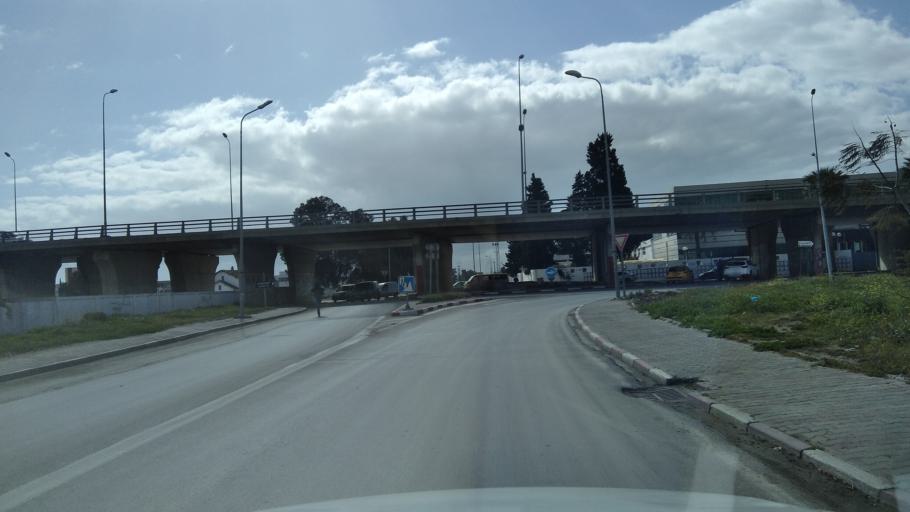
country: TN
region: Bin 'Arus
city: Ben Arous
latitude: 36.7420
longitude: 10.2270
